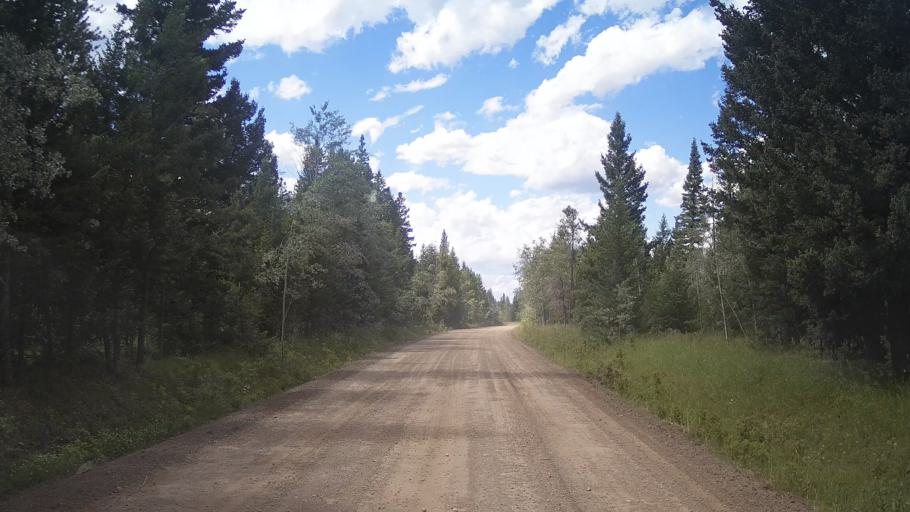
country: CA
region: British Columbia
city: Lillooet
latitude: 51.3270
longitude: -121.8834
